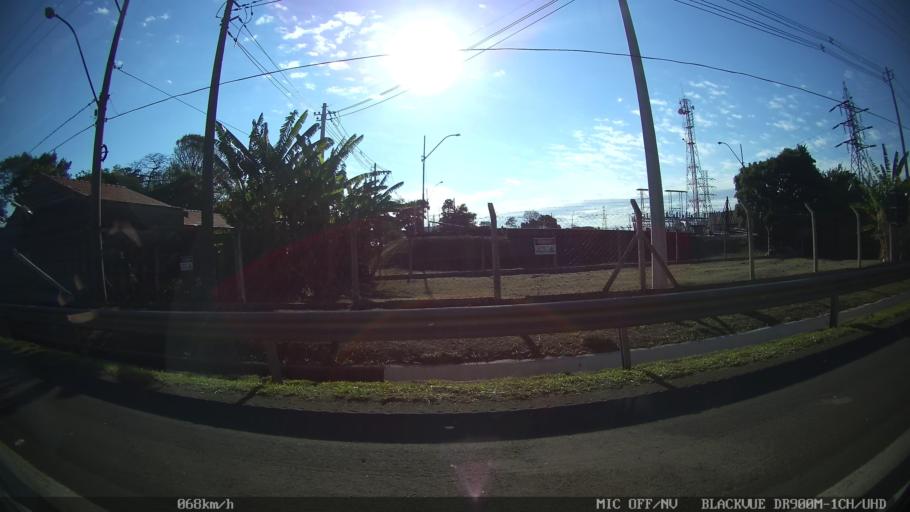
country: BR
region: Sao Paulo
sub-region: Piracicaba
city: Piracicaba
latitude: -22.6942
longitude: -47.6492
